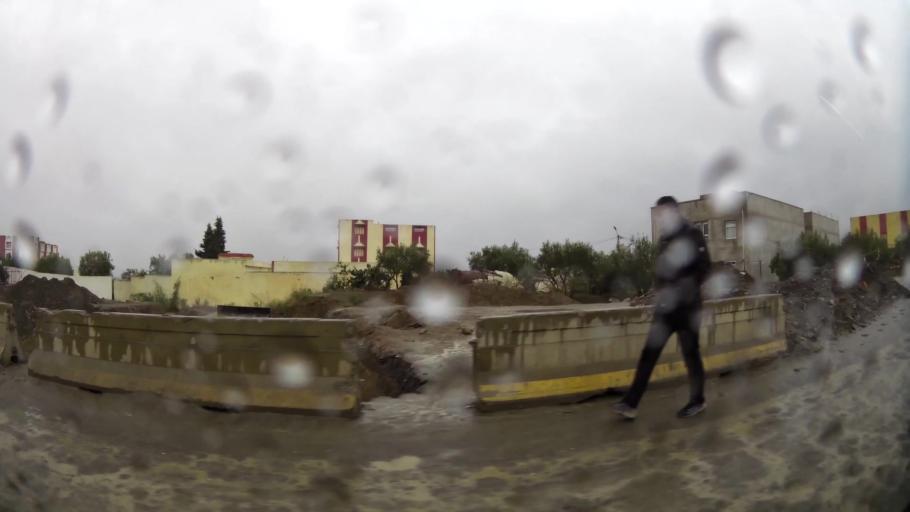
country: MA
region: Oriental
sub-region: Nador
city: Midar
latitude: 34.8719
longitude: -3.7258
